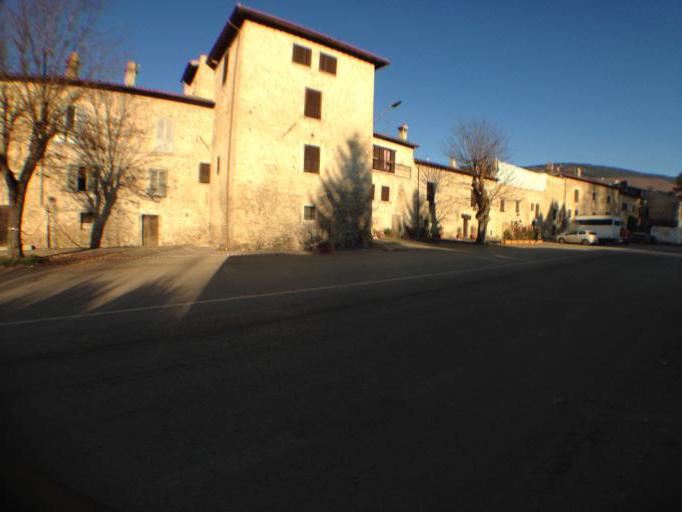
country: IT
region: Umbria
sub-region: Provincia di Perugia
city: Norcia
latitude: 42.7911
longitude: 13.0942
